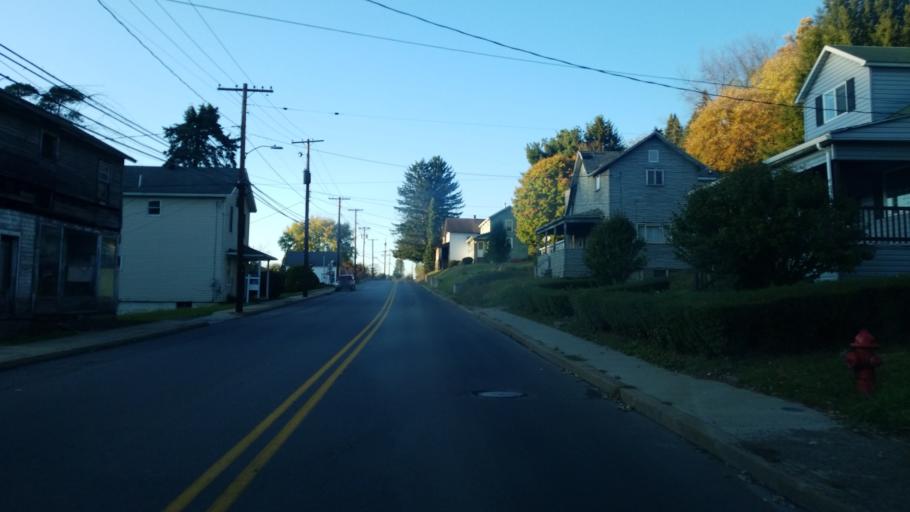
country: US
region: Pennsylvania
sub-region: Jefferson County
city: Punxsutawney
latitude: 40.9550
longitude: -78.9646
